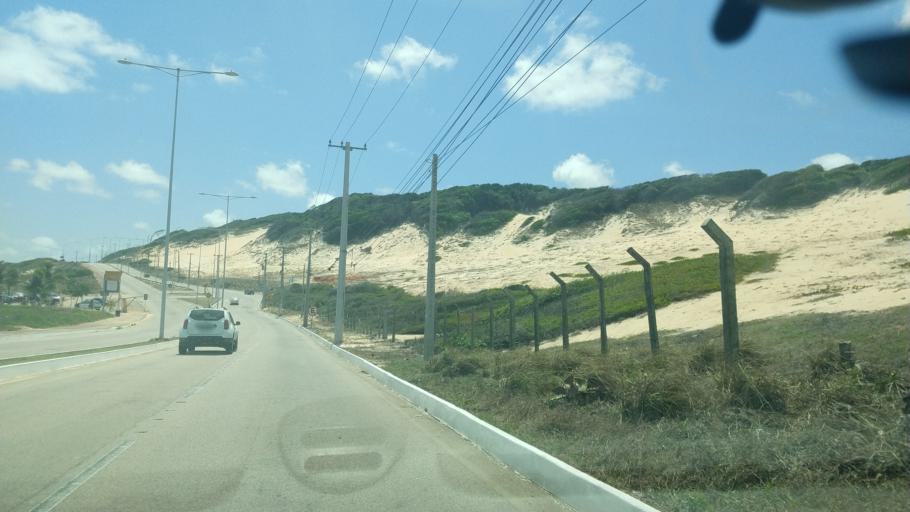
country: BR
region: Rio Grande do Norte
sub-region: Natal
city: Natal
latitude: -5.8153
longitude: -35.1826
